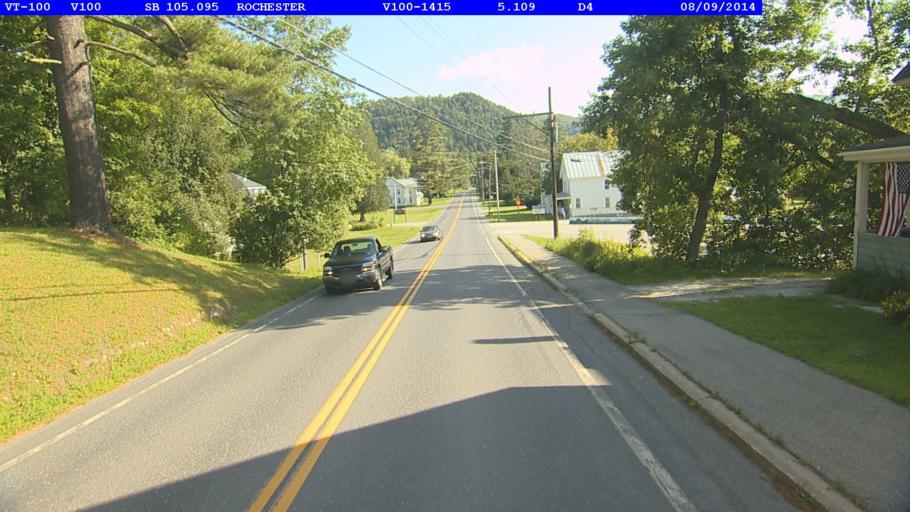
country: US
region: Vermont
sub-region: Orange County
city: Randolph
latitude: 43.8720
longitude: -72.8081
